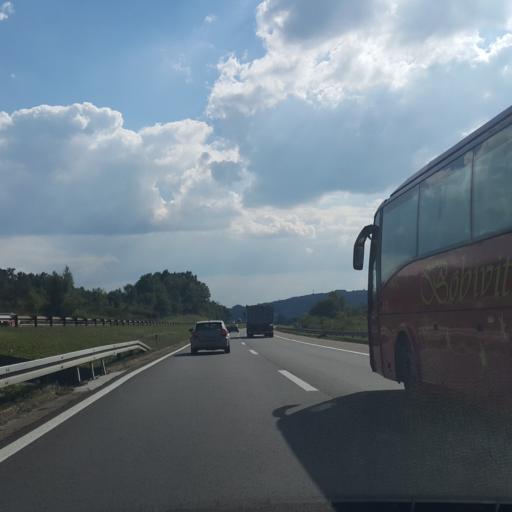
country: RS
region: Central Serbia
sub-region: Belgrade
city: Sopot
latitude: 44.6010
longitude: 20.6400
